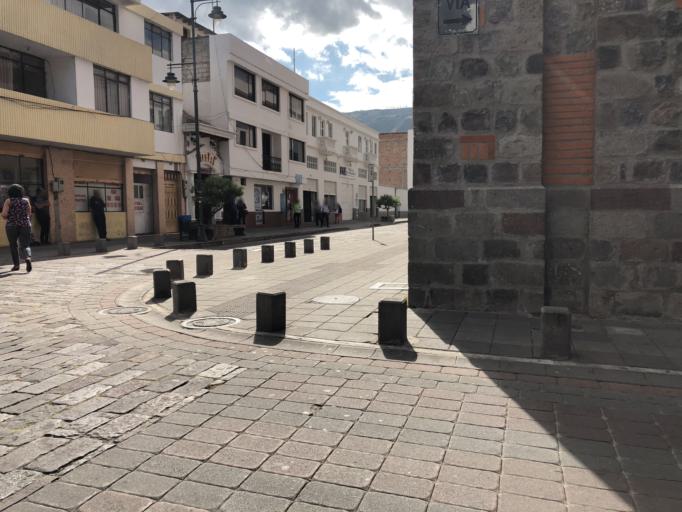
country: EC
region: Imbabura
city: Ibarra
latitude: 0.3518
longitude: -78.1192
